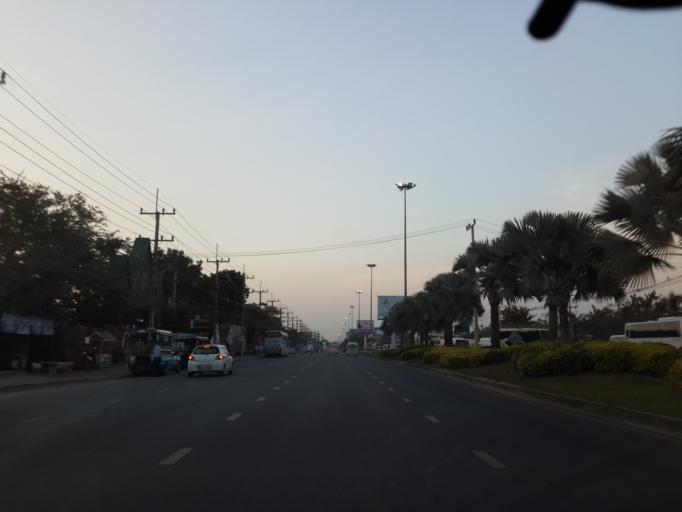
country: TH
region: Chon Buri
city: Phatthaya
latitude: 12.8670
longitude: 100.9046
